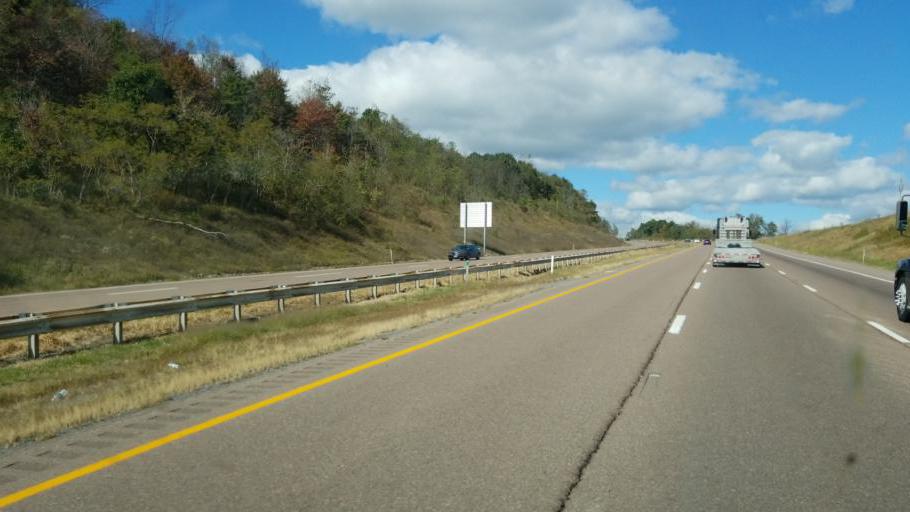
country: US
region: Maryland
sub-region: Allegany County
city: Frostburg
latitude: 39.6515
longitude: -78.9546
